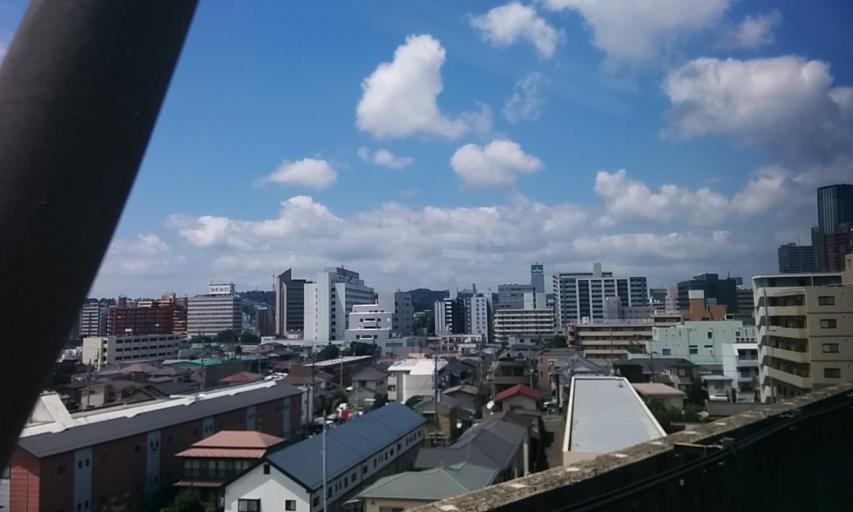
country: JP
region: Miyagi
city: Sendai
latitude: 38.2512
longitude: 140.8871
